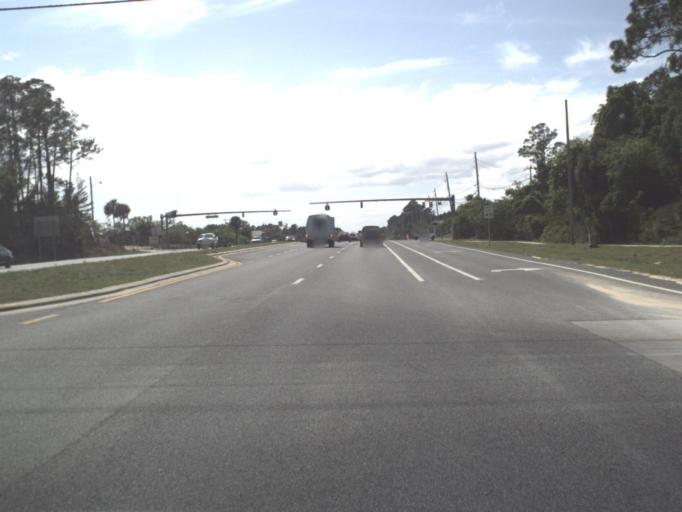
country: US
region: Florida
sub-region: Flagler County
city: Flagler Beach
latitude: 29.4766
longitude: -81.1441
